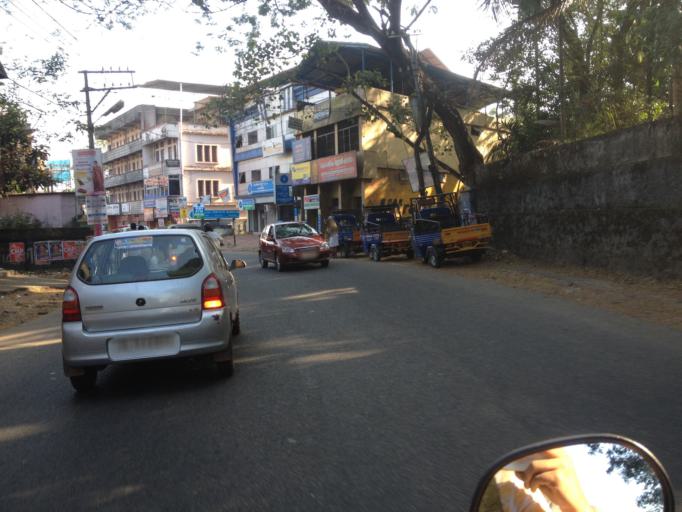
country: IN
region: Kerala
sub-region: Kollam
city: Punalur
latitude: 9.0017
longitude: 76.7728
